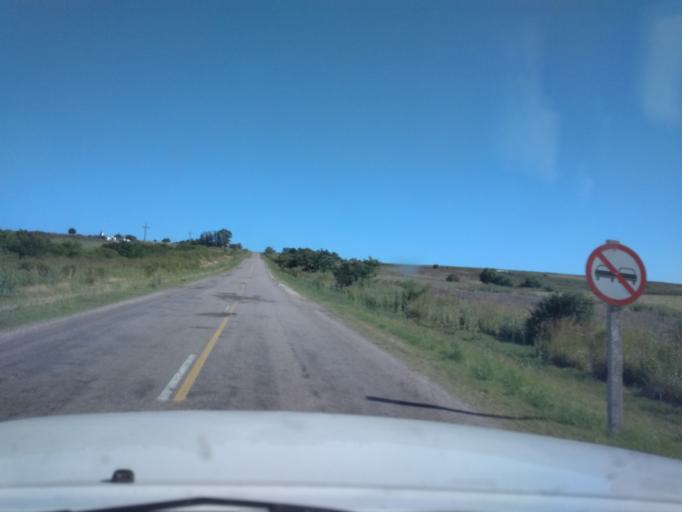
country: UY
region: Canelones
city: San Ramon
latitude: -34.1722
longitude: -55.9442
